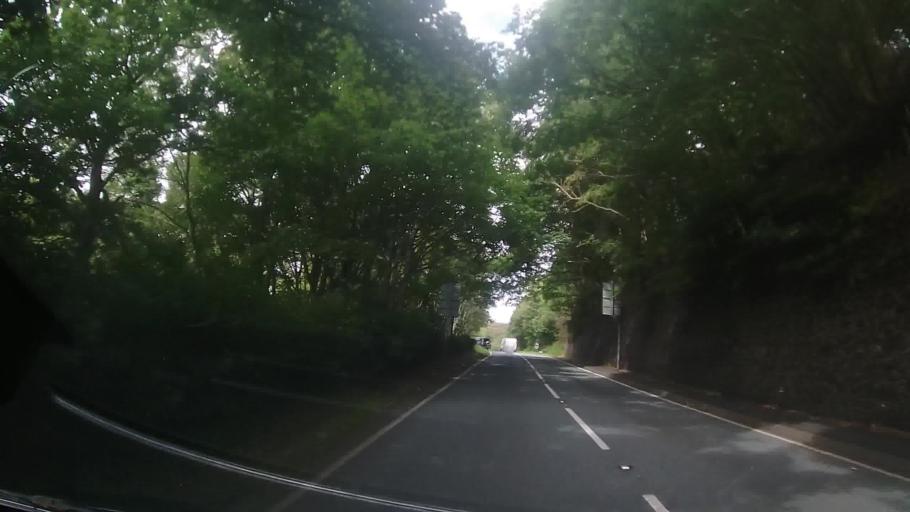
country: GB
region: Wales
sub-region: Gwynedd
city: Barmouth
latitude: 52.7154
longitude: -4.0036
